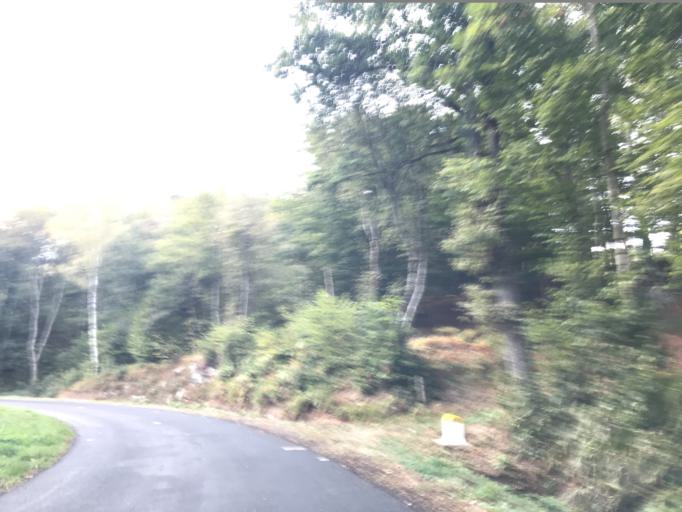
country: FR
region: Auvergne
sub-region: Departement du Puy-de-Dome
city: Celles-sur-Durolle
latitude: 45.7892
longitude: 3.6620
